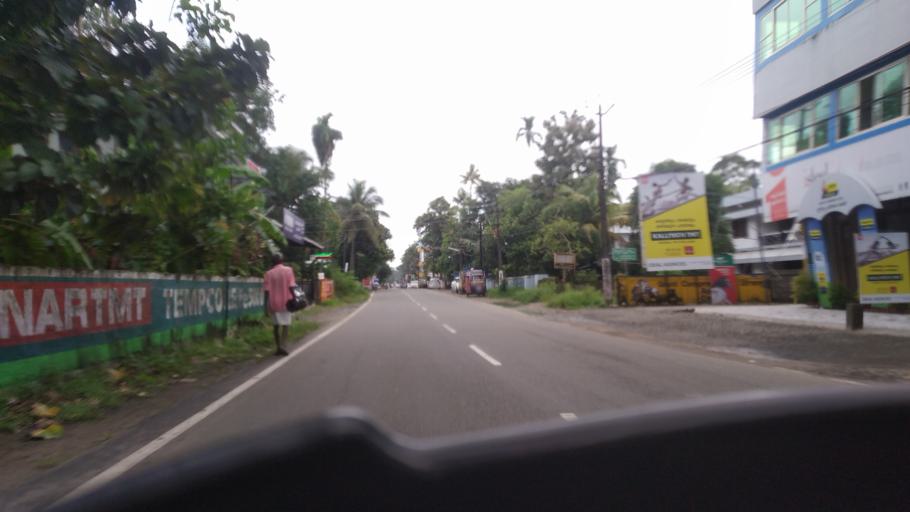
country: IN
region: Kerala
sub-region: Ernakulam
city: Elur
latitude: 10.0957
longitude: 76.2064
